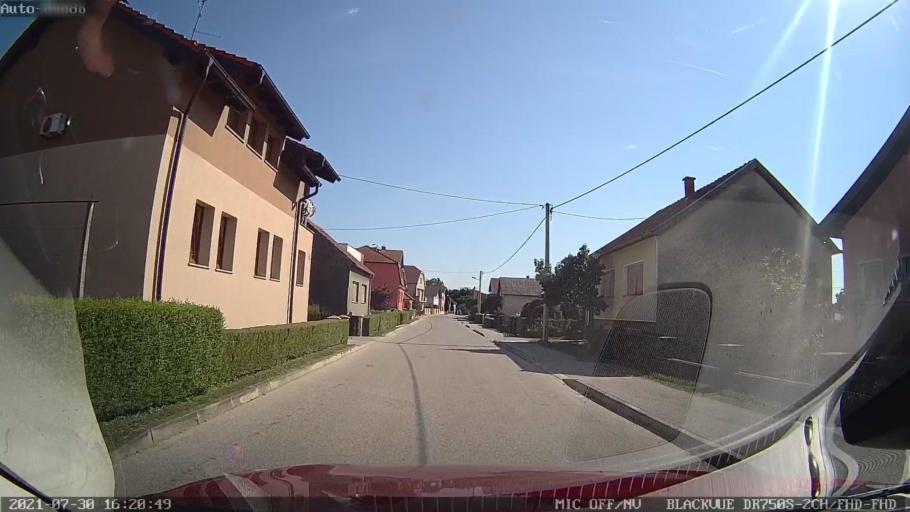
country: HR
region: Medimurska
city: Kursanec
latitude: 46.2977
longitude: 16.4076
